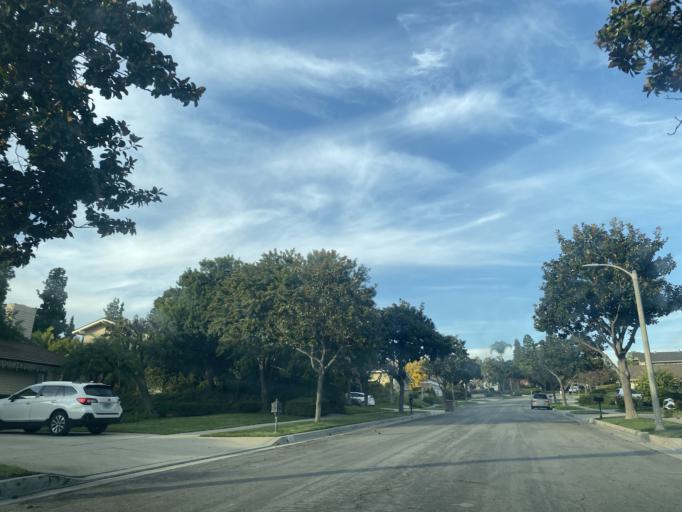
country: US
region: California
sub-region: Orange County
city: Placentia
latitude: 33.8856
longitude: -117.8958
